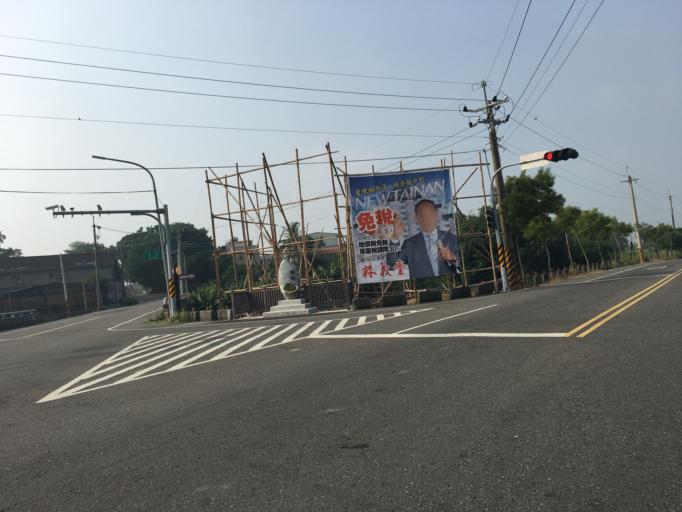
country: TW
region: Taiwan
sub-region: Chiayi
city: Taibao
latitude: 23.3861
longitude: 120.3367
